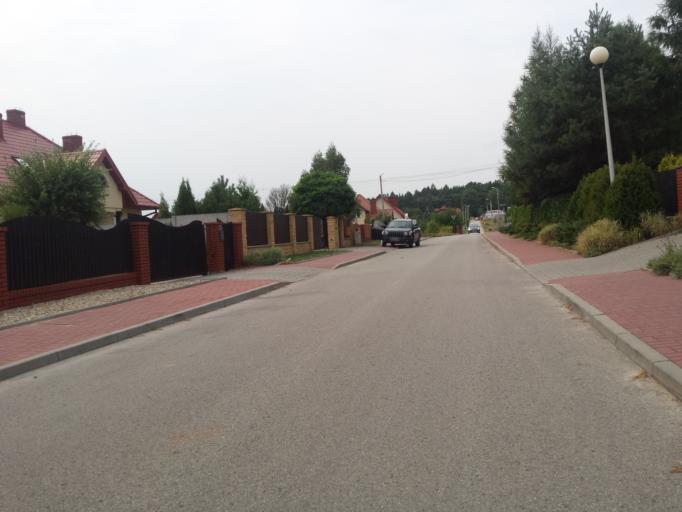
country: PL
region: Swietokrzyskie
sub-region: Powiat kielecki
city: Morawica
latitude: 50.7689
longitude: 20.6245
